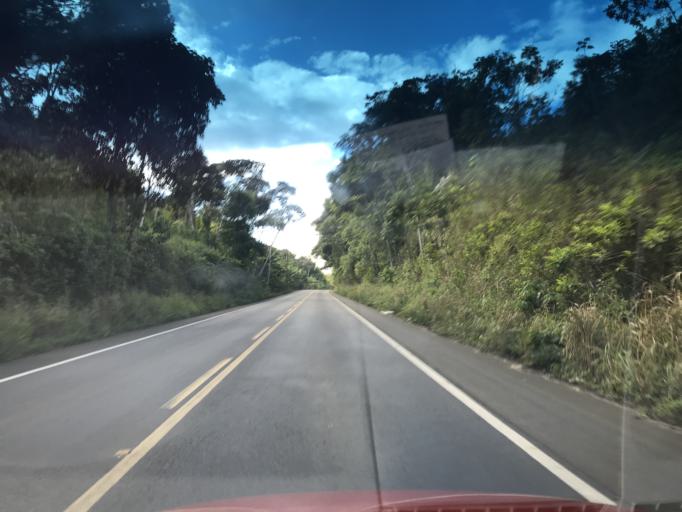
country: BR
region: Bahia
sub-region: Ibirapitanga
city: Ibirapitanga
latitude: -14.1924
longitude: -39.3153
